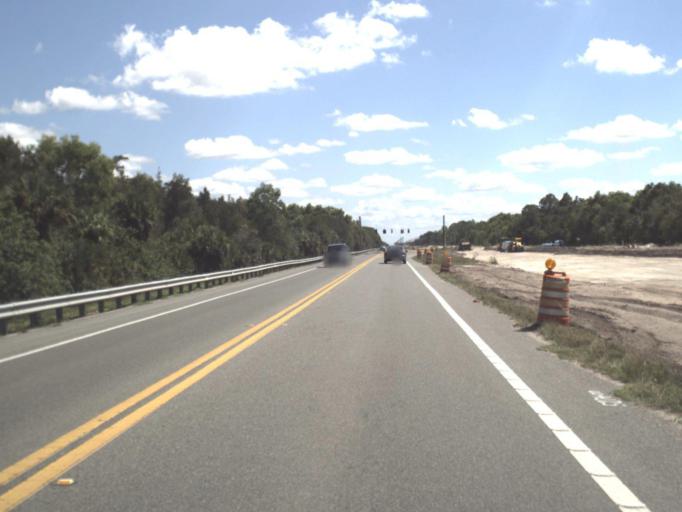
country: US
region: Florida
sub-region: Collier County
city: Lely Resort
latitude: 26.0511
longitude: -81.6799
